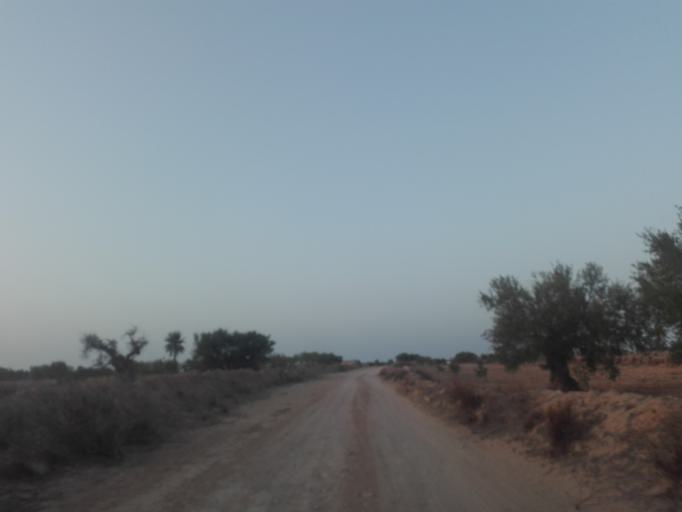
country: TN
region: Madanin
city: Houmt Souk
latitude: 33.7512
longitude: 10.7702
